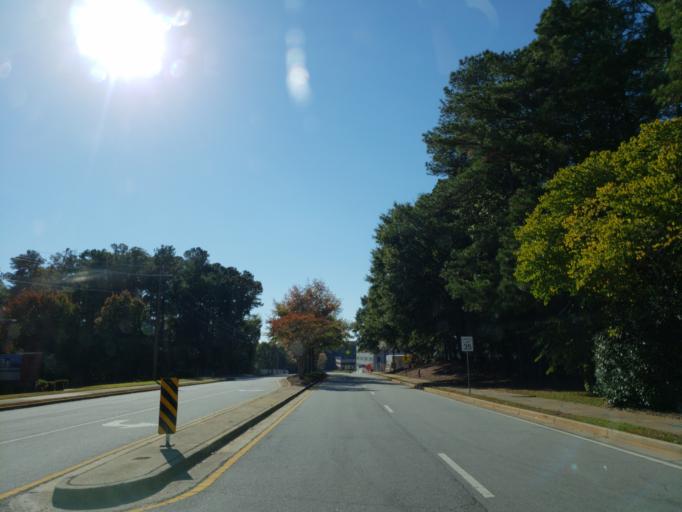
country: US
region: Georgia
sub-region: Gwinnett County
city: Lawrenceville
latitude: 33.9502
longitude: -83.9907
